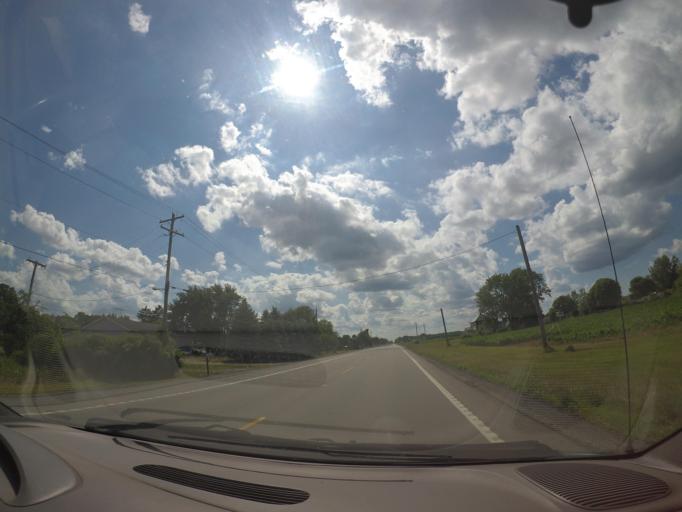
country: US
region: Ohio
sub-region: Huron County
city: Norwalk
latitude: 41.2493
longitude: -82.5478
